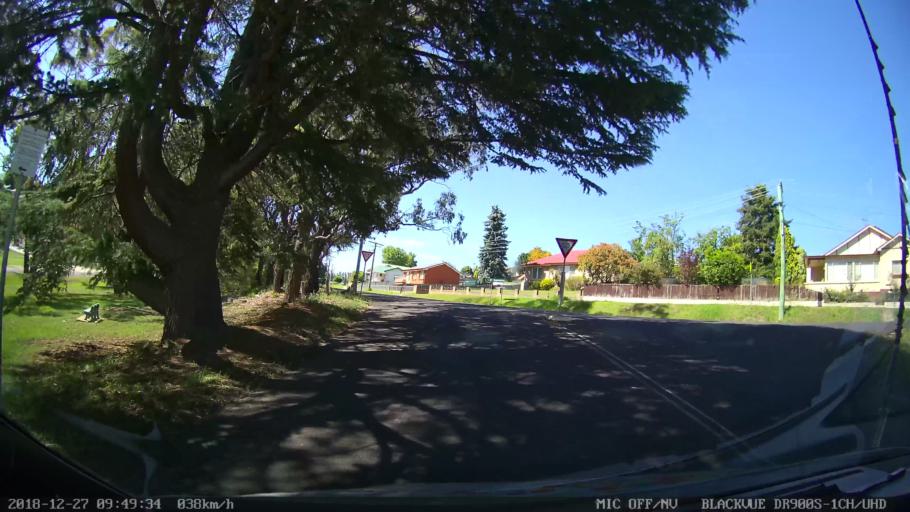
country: AU
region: New South Wales
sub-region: Lithgow
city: Portland
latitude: -33.3549
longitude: 149.9819
